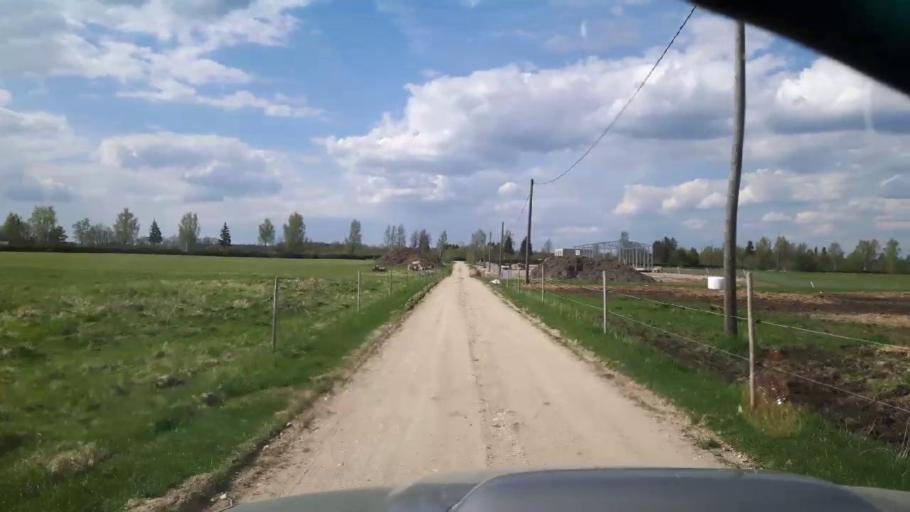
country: EE
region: Paernumaa
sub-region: Sindi linn
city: Sindi
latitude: 58.4253
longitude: 24.7285
